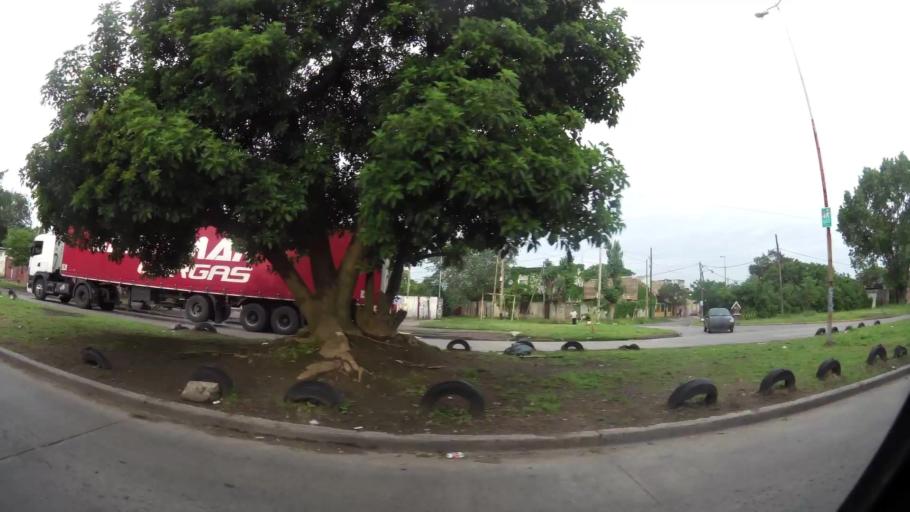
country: AR
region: Buenos Aires
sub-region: Partido de Lanus
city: Lanus
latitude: -34.7304
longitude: -58.3460
